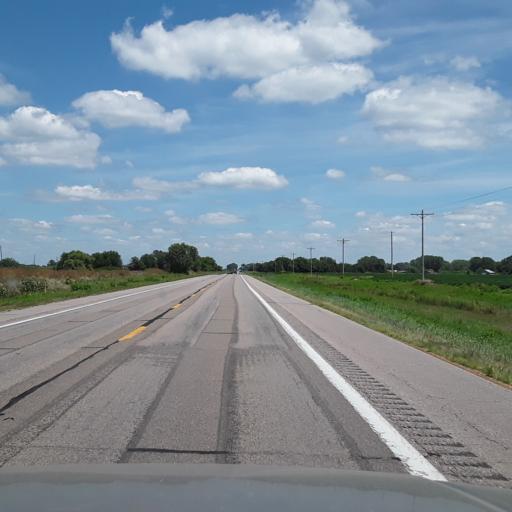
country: US
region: Nebraska
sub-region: Nance County
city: Genoa
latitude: 41.3387
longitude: -97.6099
